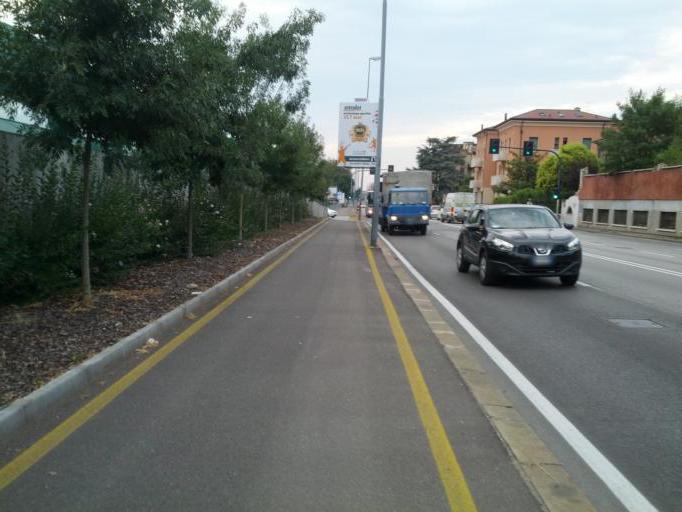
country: IT
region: Veneto
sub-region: Provincia di Verona
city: Poiano
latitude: 45.4367
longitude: 11.0295
